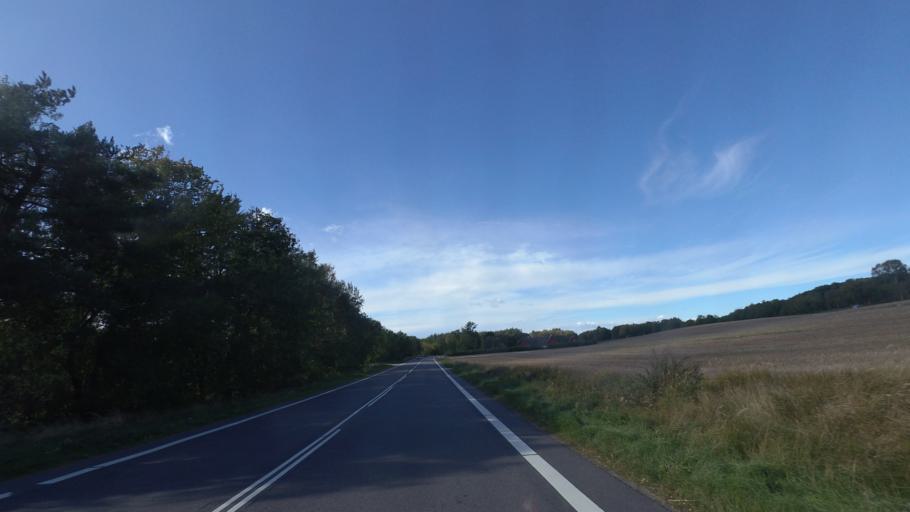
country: DK
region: Capital Region
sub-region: Bornholm Kommune
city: Ronne
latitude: 55.0793
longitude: 14.7608
